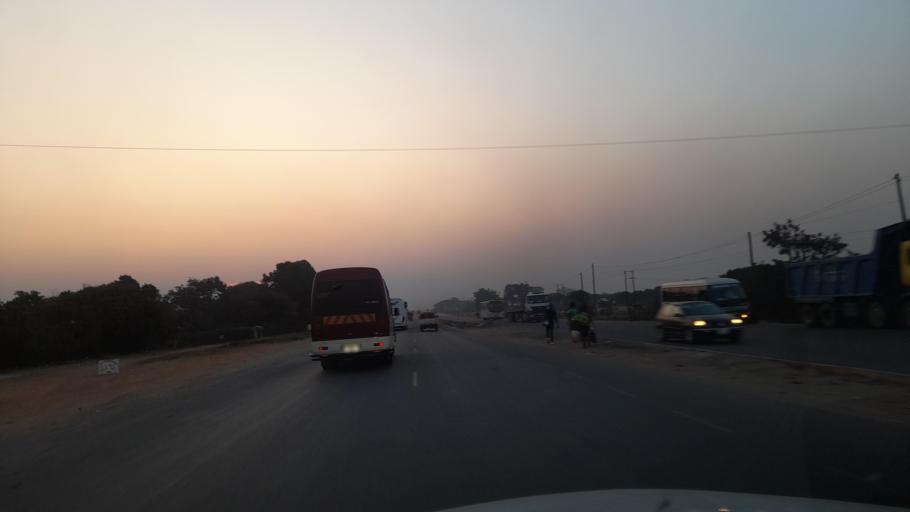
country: ZM
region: Copperbelt
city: Kitwe
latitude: -12.7744
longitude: 28.1897
